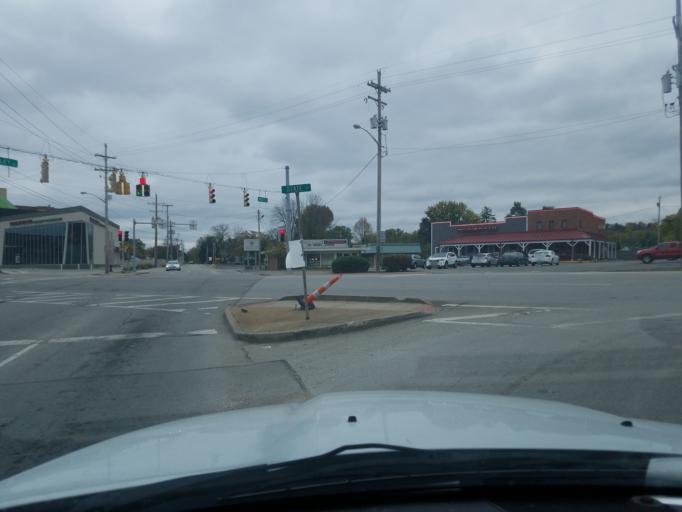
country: US
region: Indiana
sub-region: Floyd County
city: New Albany
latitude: 38.3021
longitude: -85.8366
